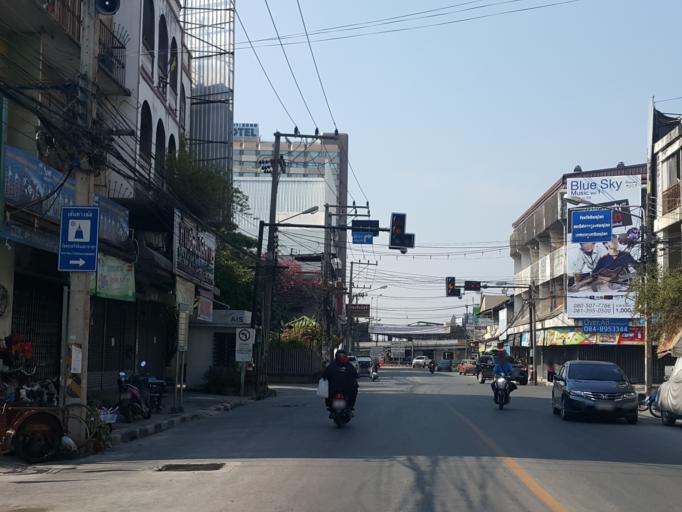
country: TH
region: Phitsanulok
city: Phitsanulok
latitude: 16.8194
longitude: 100.2651
